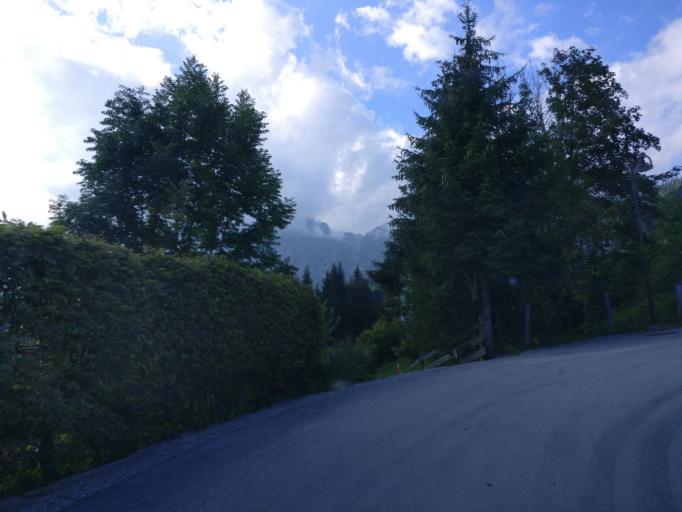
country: AT
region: Salzburg
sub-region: Politischer Bezirk Sankt Johann im Pongau
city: Muhlbach am Hochkonig
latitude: 47.3795
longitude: 13.1266
